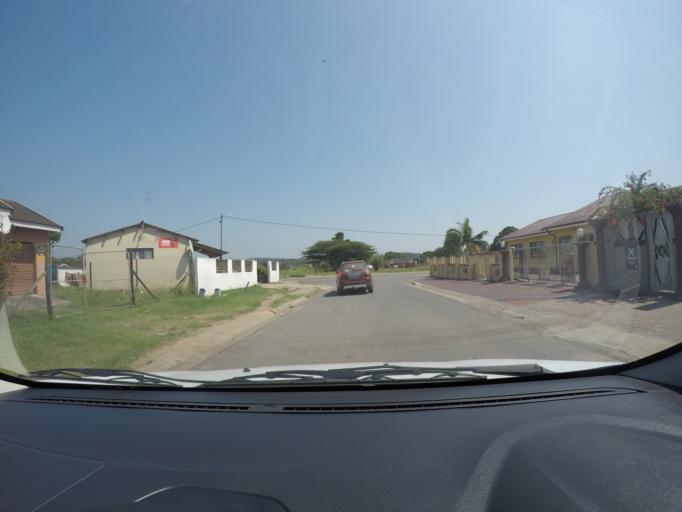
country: ZA
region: KwaZulu-Natal
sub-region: uThungulu District Municipality
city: eSikhawini
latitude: -28.8666
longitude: 31.9147
